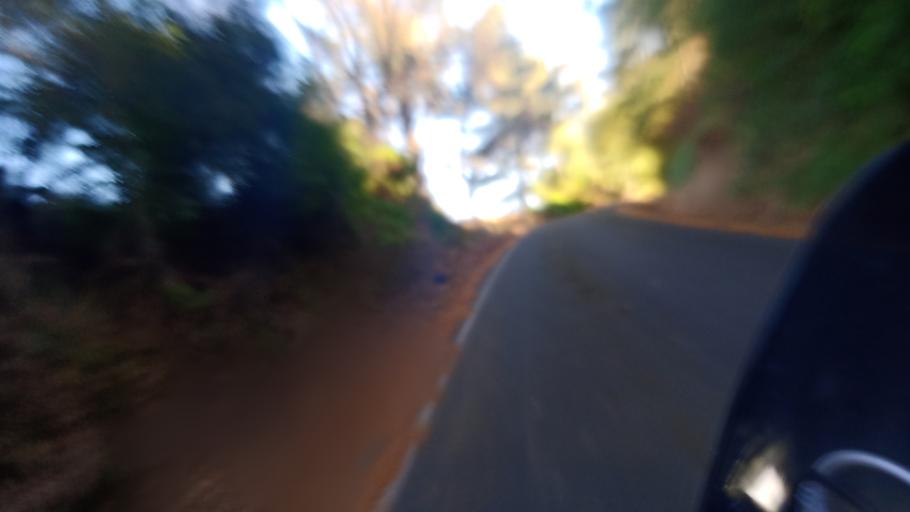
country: NZ
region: Hawke's Bay
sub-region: Wairoa District
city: Wairoa
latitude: -38.8777
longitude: 177.2357
